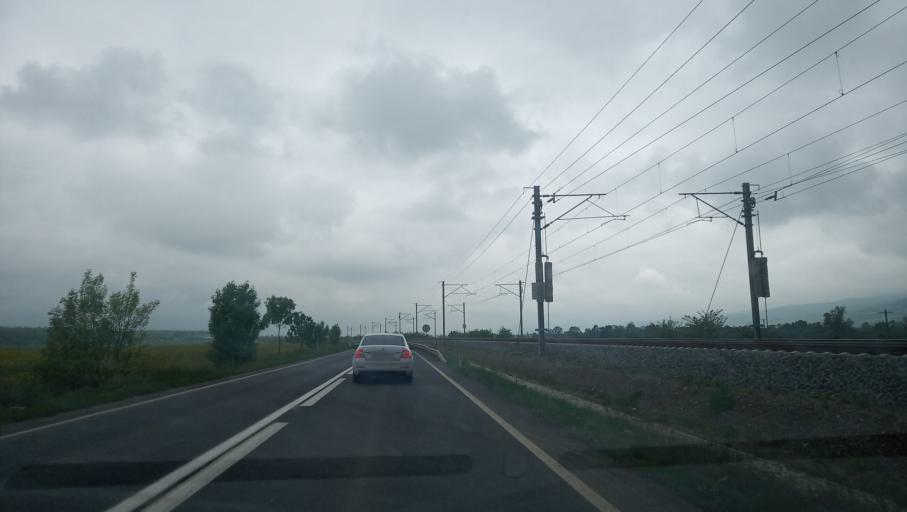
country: RO
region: Alba
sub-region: Comuna Saliste
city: Salistea
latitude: 45.9417
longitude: 23.3884
